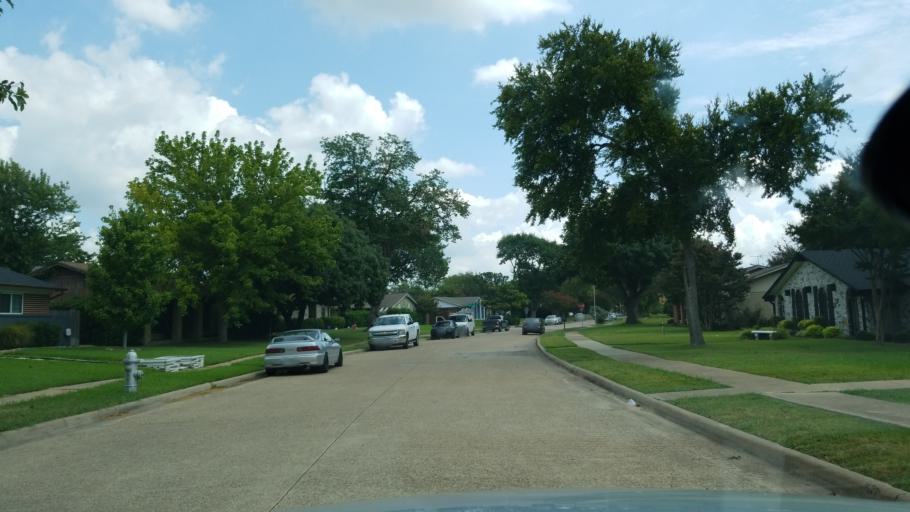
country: US
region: Texas
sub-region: Dallas County
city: Garland
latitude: 32.9267
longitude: -96.6541
